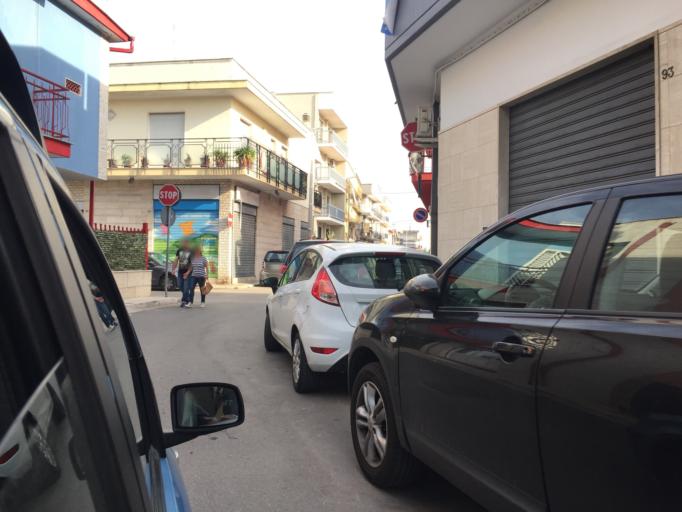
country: IT
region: Apulia
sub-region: Provincia di Bari
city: Capurso
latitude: 41.0455
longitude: 16.9211
